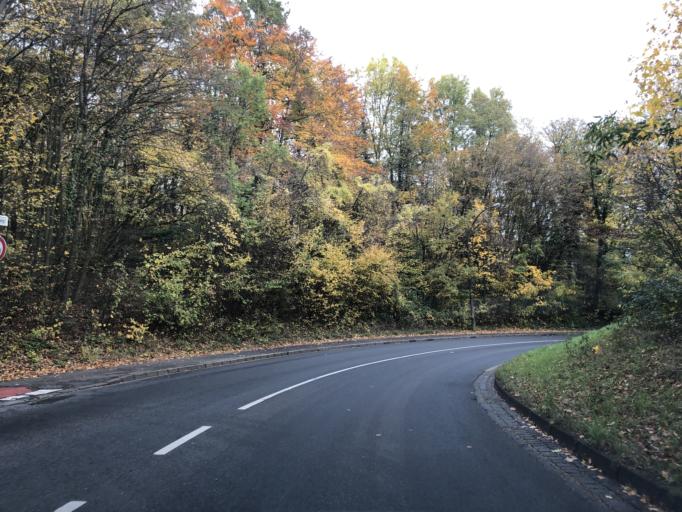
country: DE
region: North Rhine-Westphalia
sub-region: Regierungsbezirk Koln
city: Konigswinter
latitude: 50.6709
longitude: 7.1498
